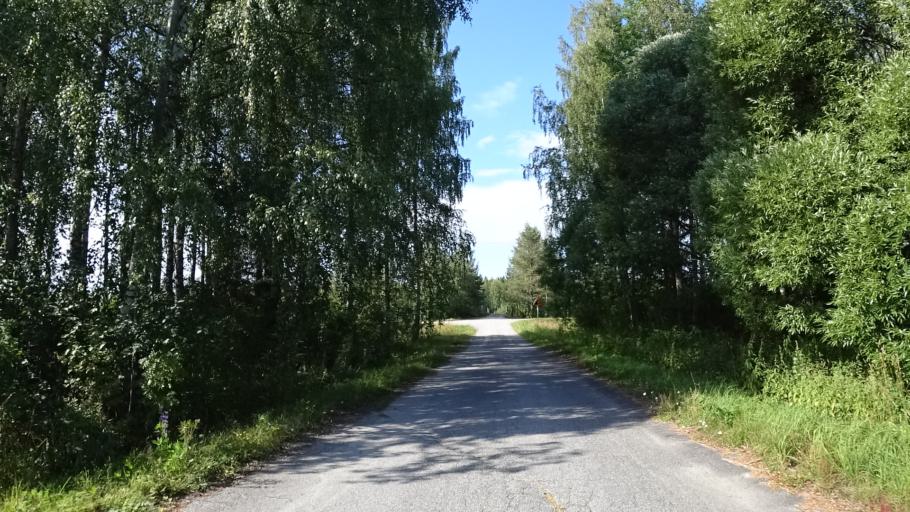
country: FI
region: North Karelia
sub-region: Joensuu
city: Eno
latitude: 62.8005
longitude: 30.1491
